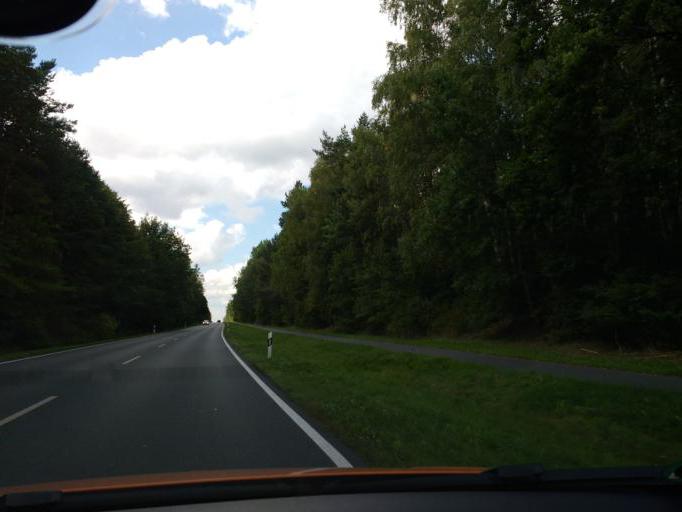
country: DE
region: Brandenburg
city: Wandlitz
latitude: 52.7394
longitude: 13.4709
